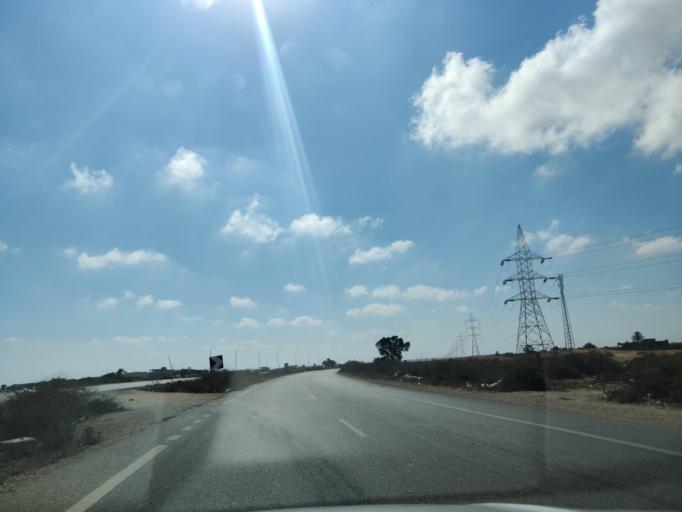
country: EG
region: Muhafazat Matruh
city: Al `Alamayn
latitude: 31.0548
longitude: 28.3093
